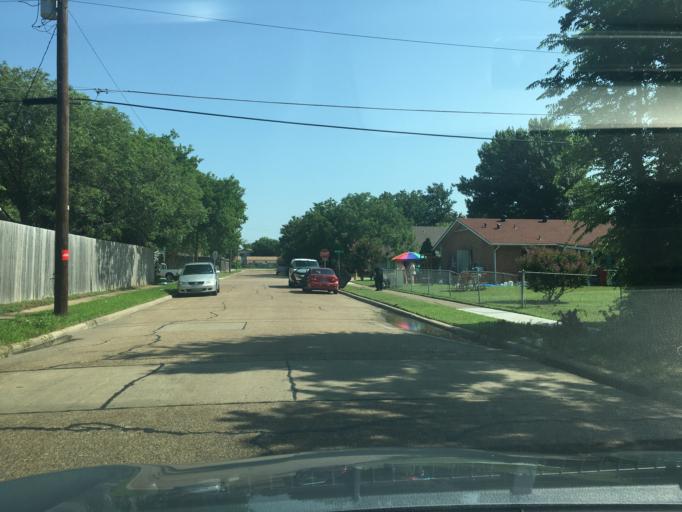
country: US
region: Texas
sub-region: Dallas County
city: Richardson
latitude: 32.9274
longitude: -96.6973
